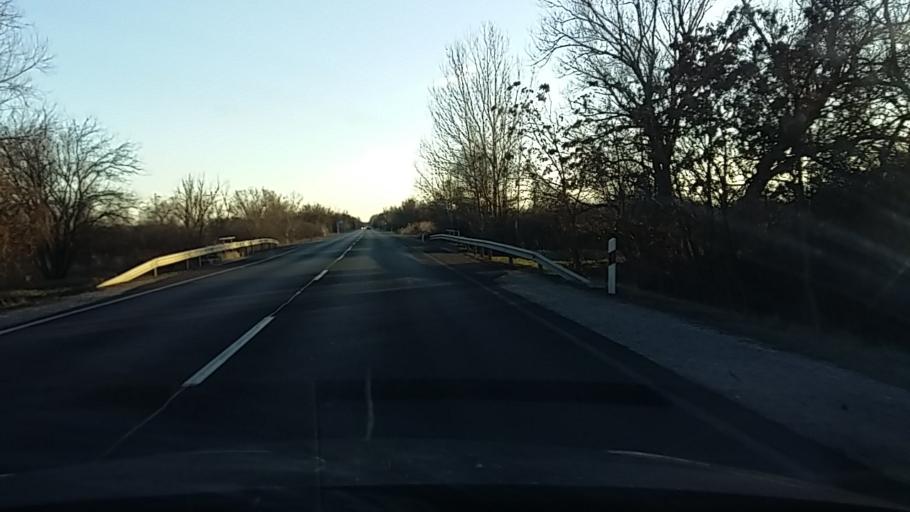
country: HU
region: Szabolcs-Szatmar-Bereg
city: Ujfeherto
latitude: 47.8532
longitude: 21.7039
